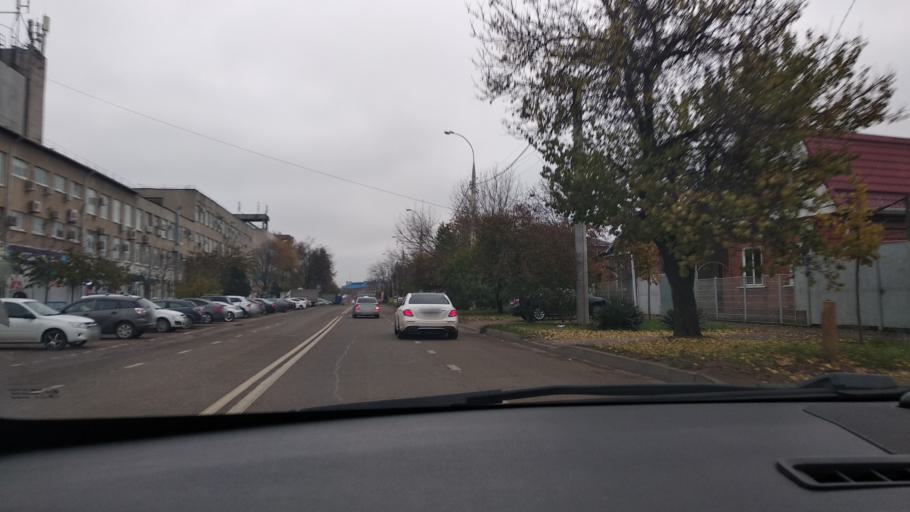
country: RU
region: Krasnodarskiy
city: Krasnodar
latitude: 45.0282
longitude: 39.0204
